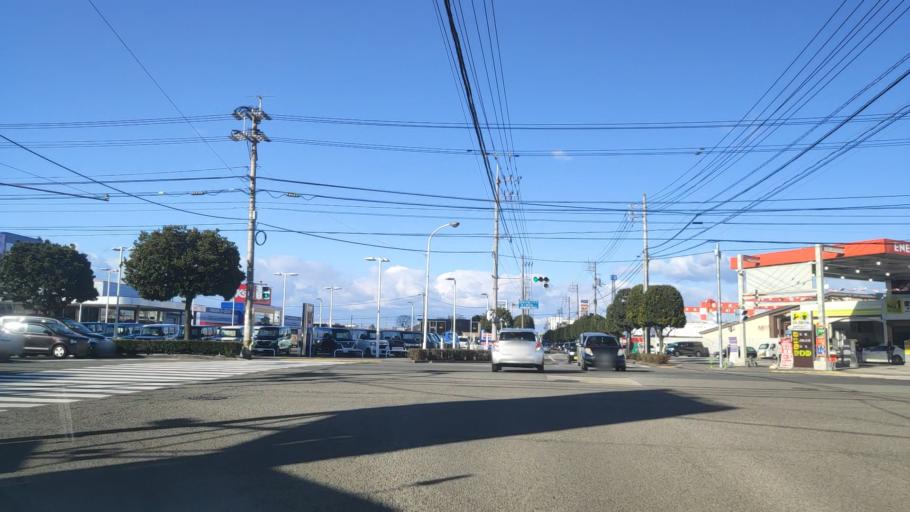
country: JP
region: Ehime
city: Saijo
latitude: 33.9292
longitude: 133.1902
